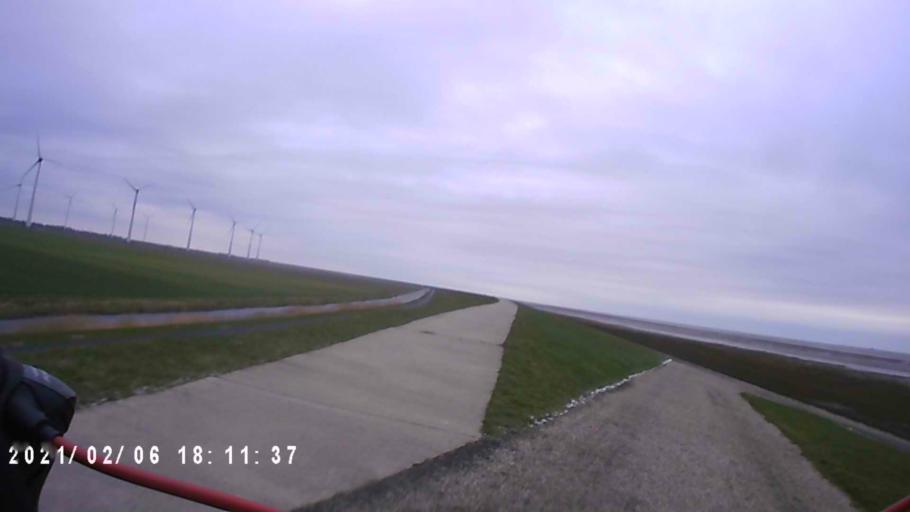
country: DE
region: Lower Saxony
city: Borkum
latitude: 53.4597
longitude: 6.7809
